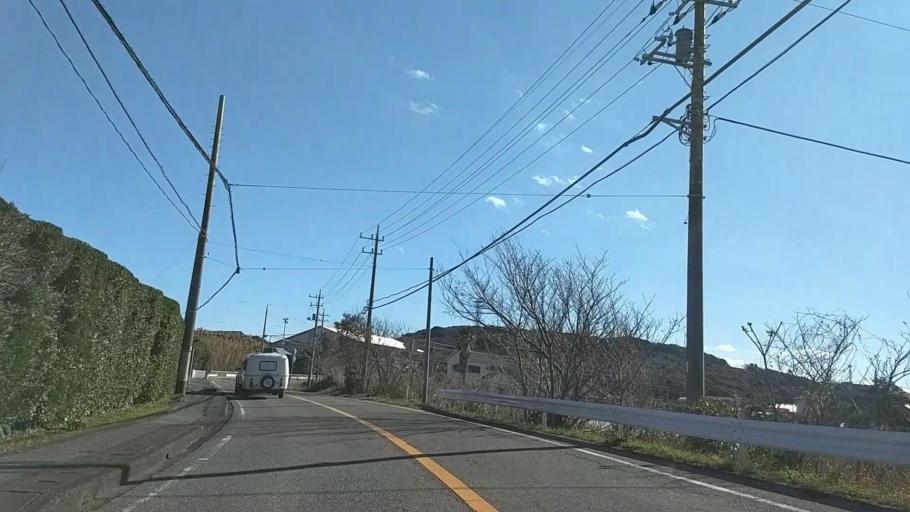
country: JP
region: Chiba
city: Tateyama
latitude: 34.9419
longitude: 139.8382
